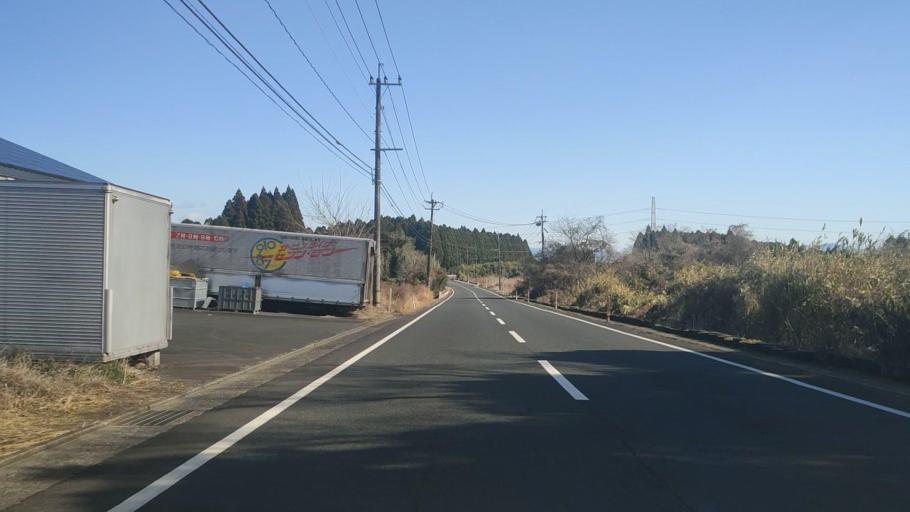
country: JP
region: Kagoshima
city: Sueyoshicho-ninokata
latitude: 31.6872
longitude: 130.9493
